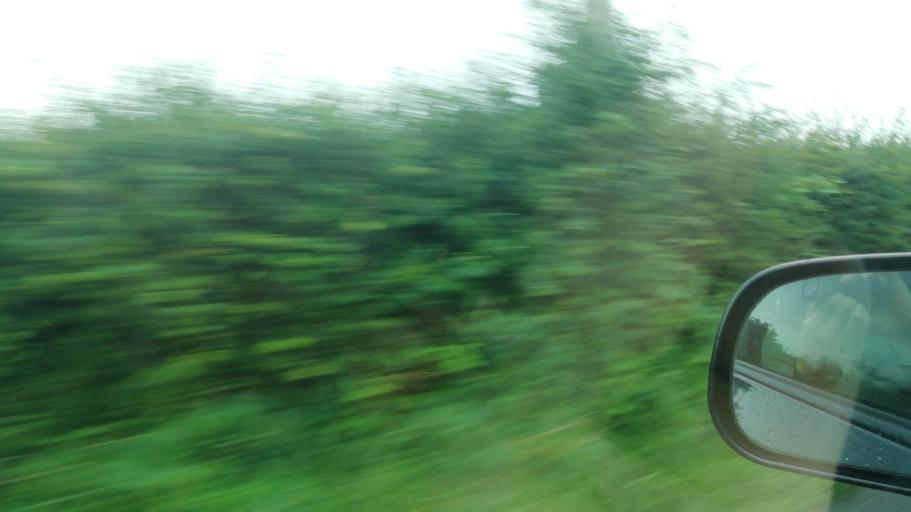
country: IE
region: Leinster
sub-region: Kilkenny
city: Thomastown
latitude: 52.6126
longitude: -7.1046
